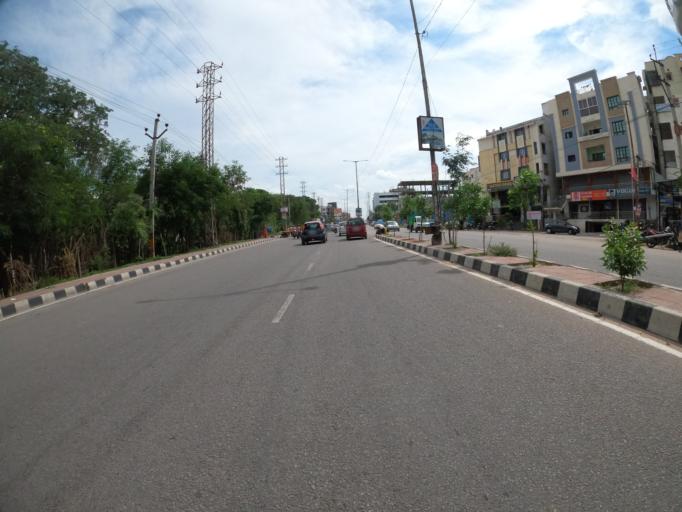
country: IN
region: Telangana
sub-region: Hyderabad
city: Hyderabad
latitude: 17.3604
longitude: 78.3891
